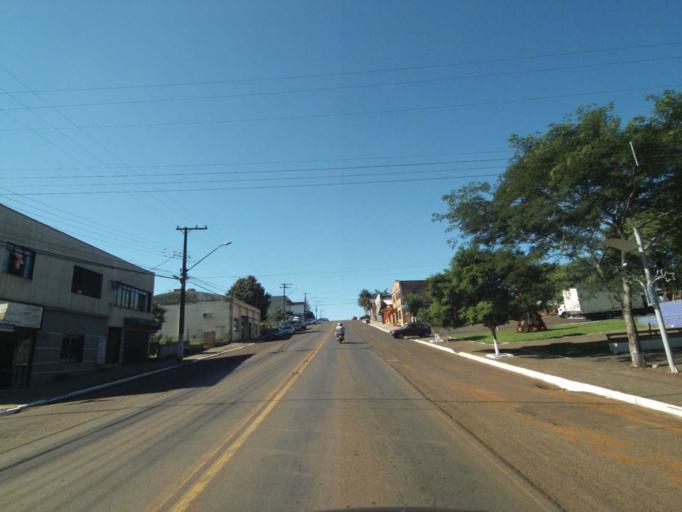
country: BR
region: Parana
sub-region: Coronel Vivida
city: Coronel Vivida
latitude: -25.9606
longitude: -52.8154
